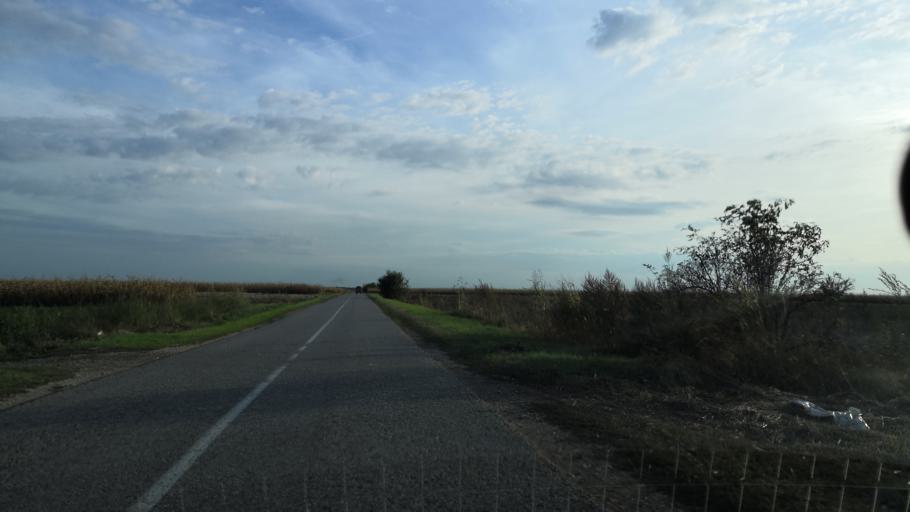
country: RS
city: Novi Karlovci
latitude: 45.0633
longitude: 20.1802
